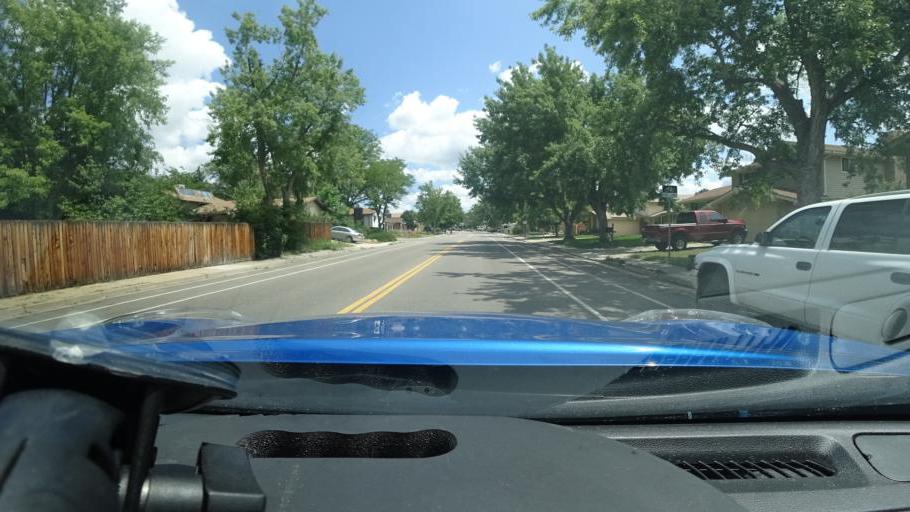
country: US
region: Colorado
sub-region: Adams County
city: Aurora
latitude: 39.7018
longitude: -104.8390
